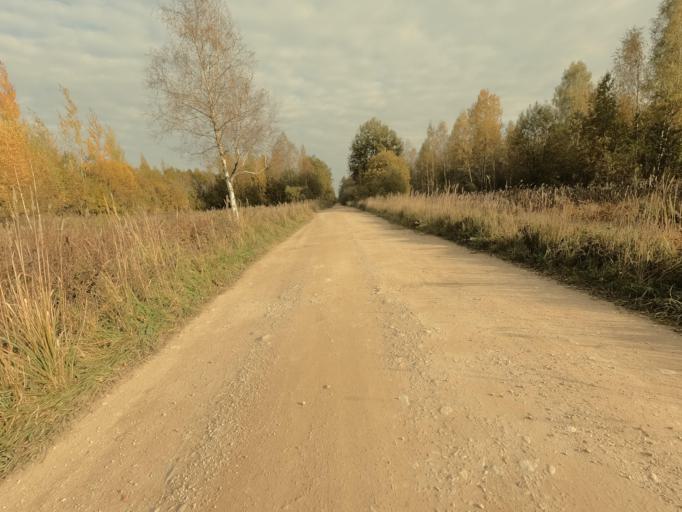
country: RU
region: Novgorod
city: Pankovka
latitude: 58.8960
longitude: 31.0066
